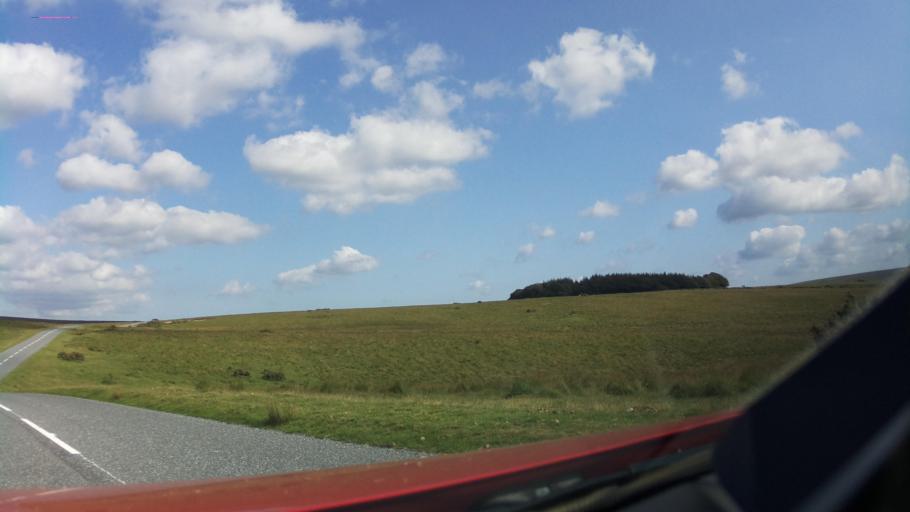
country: GB
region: England
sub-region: Devon
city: South Brent
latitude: 50.5572
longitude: -3.9306
